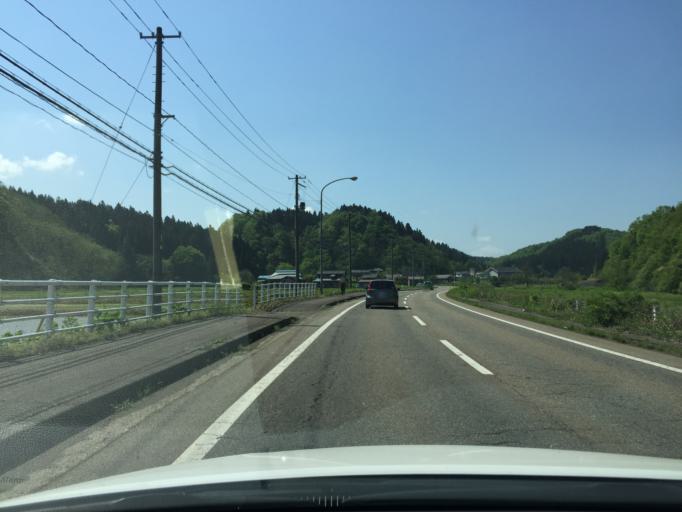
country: JP
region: Niigata
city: Kamo
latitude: 37.6213
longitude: 139.1044
